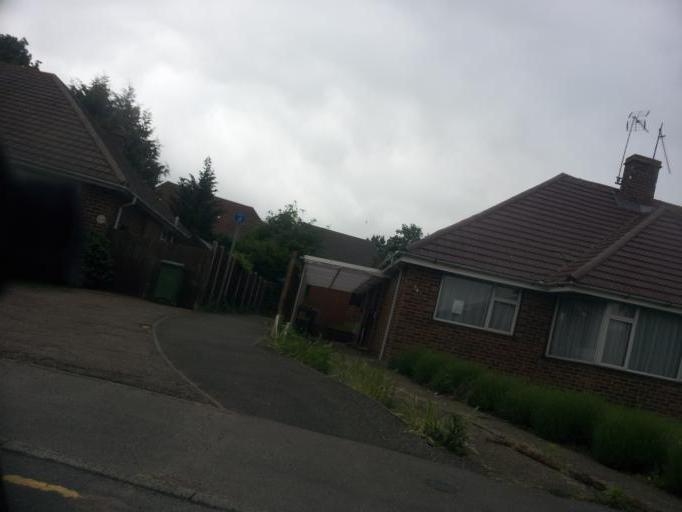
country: GB
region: England
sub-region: Kent
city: Maidstone
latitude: 51.2754
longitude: 0.4949
